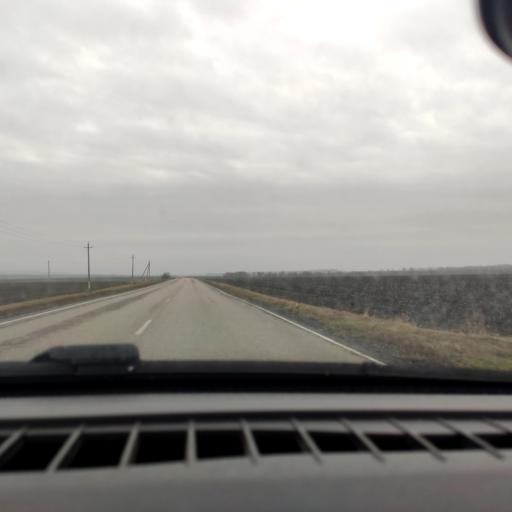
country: RU
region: Belgorod
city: Ilovka
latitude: 50.7792
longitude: 38.8047
